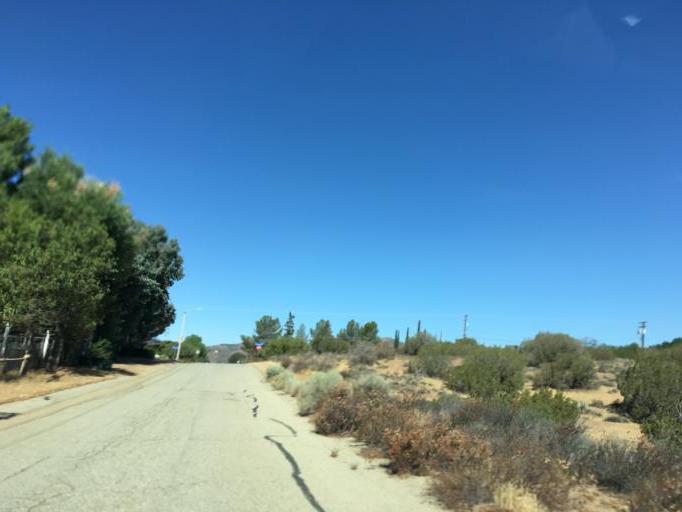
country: US
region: California
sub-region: Los Angeles County
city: Acton
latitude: 34.4845
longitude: -118.1969
